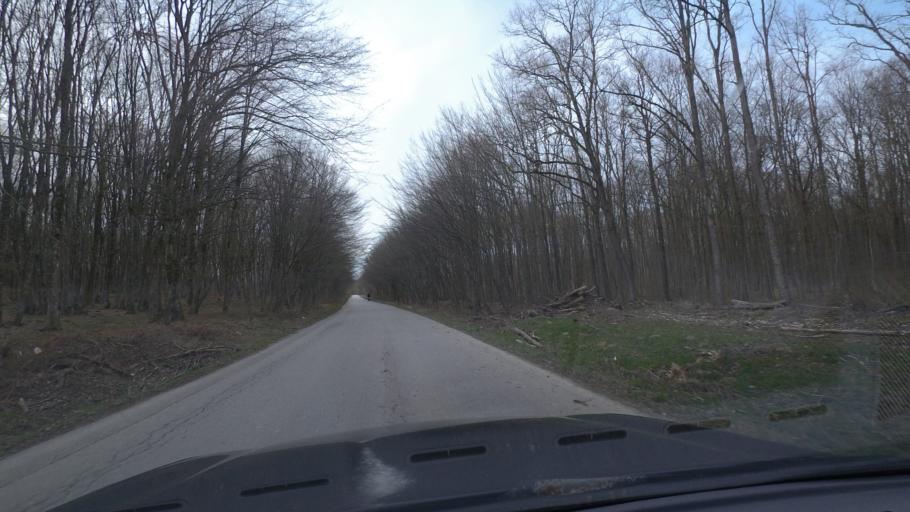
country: HR
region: Grad Zagreb
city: Horvati
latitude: 45.7026
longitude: 15.8335
